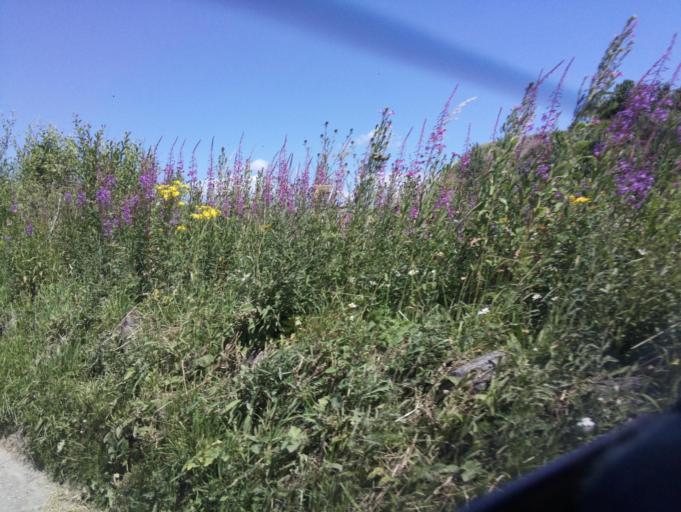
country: GB
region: England
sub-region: Derbyshire
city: Buxton
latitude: 53.2894
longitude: -1.8651
